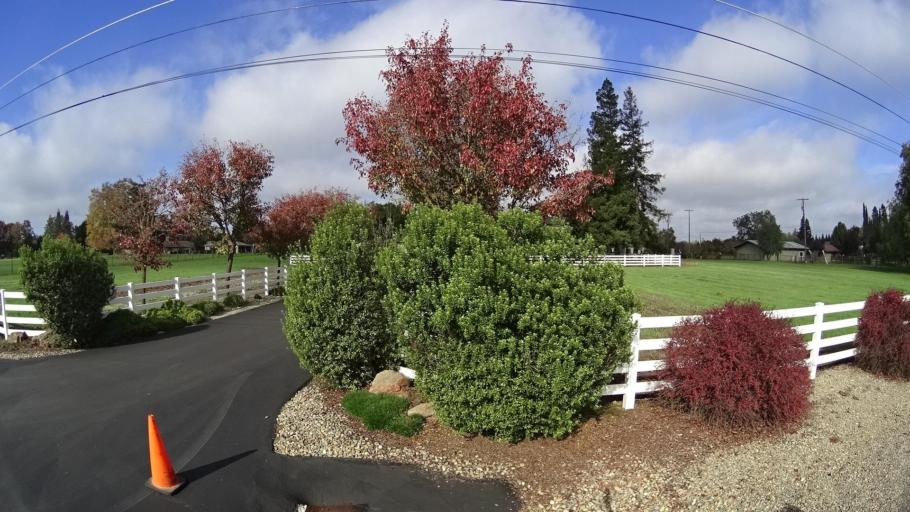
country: US
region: California
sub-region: Sacramento County
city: Vineyard
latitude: 38.4345
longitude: -121.3167
